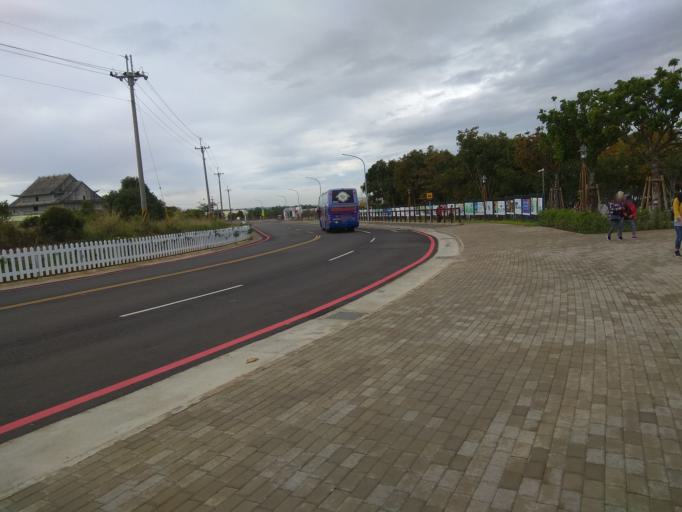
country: TW
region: Taiwan
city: Fengyuan
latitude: 24.3240
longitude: 120.6848
